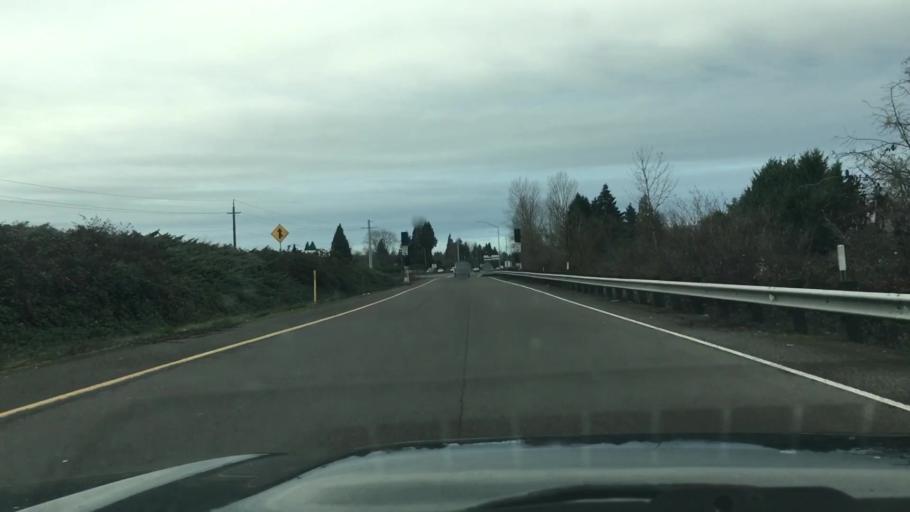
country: US
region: Oregon
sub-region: Lane County
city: Eugene
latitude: 44.0881
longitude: -123.0695
